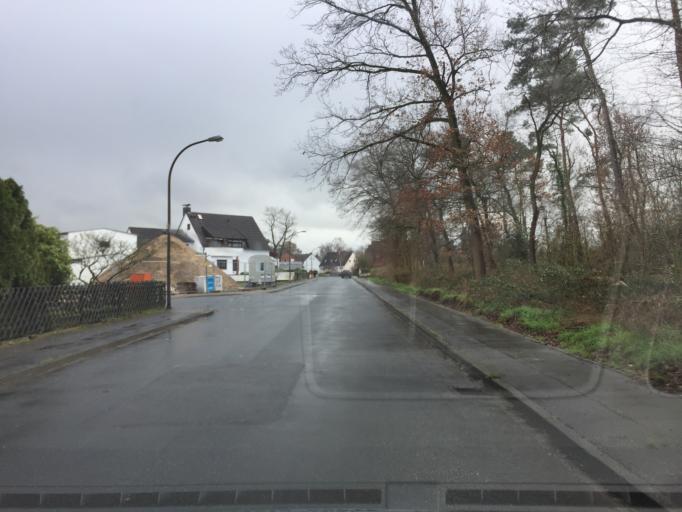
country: DE
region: Lower Saxony
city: Wunstorf
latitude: 52.4304
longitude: 9.4988
